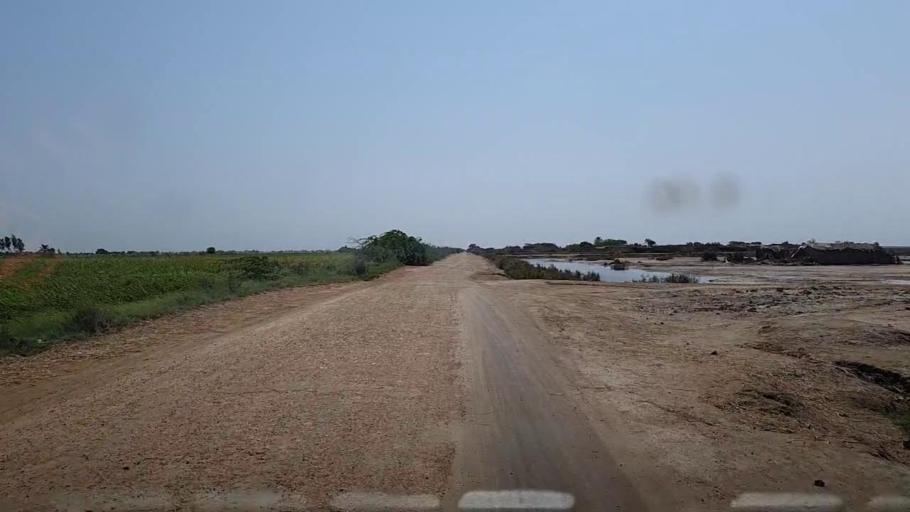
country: PK
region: Sindh
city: Mirpur Batoro
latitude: 24.6332
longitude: 68.4522
